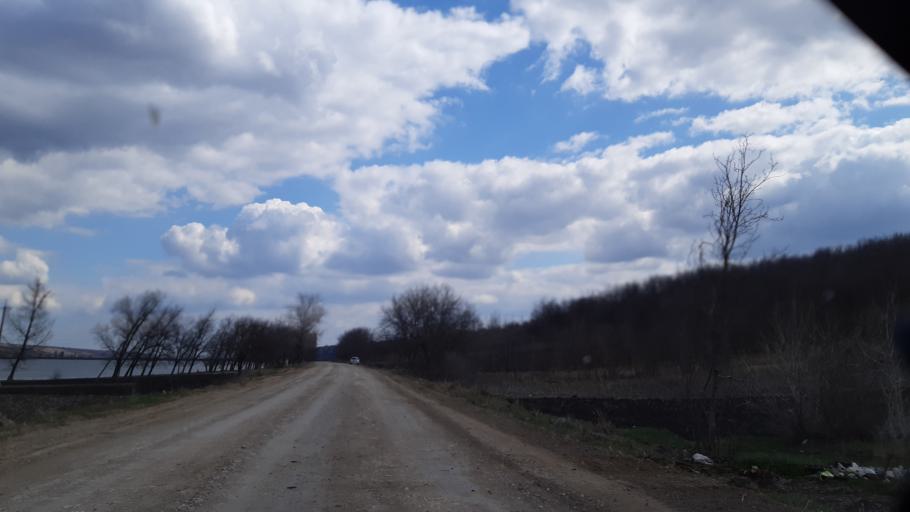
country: MD
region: Laloveni
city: Ialoveni
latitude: 46.8897
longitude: 28.7312
